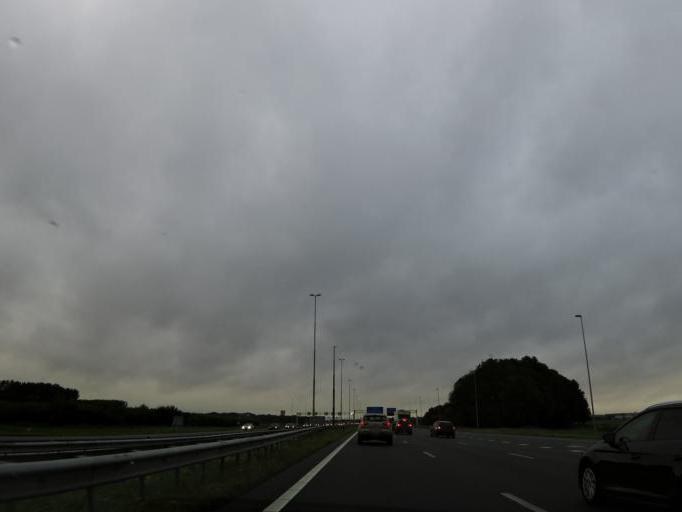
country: NL
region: Utrecht
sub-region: Gemeente Vianen
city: Vianen
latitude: 51.9674
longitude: 5.1121
